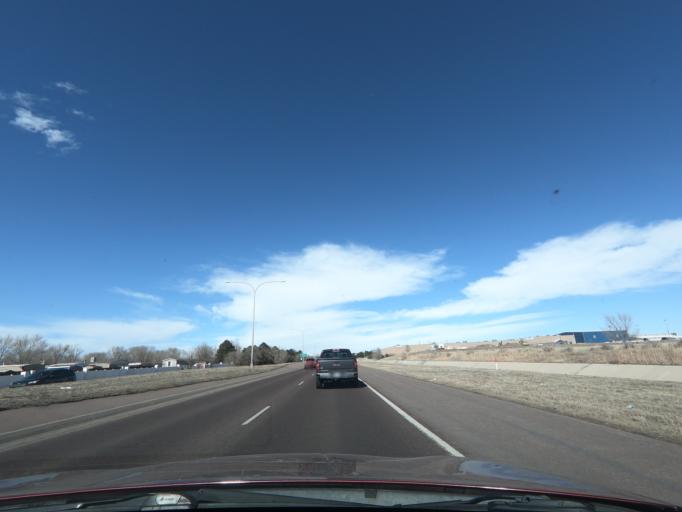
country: US
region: Colorado
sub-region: El Paso County
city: Security-Widefield
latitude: 38.7946
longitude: -104.7302
